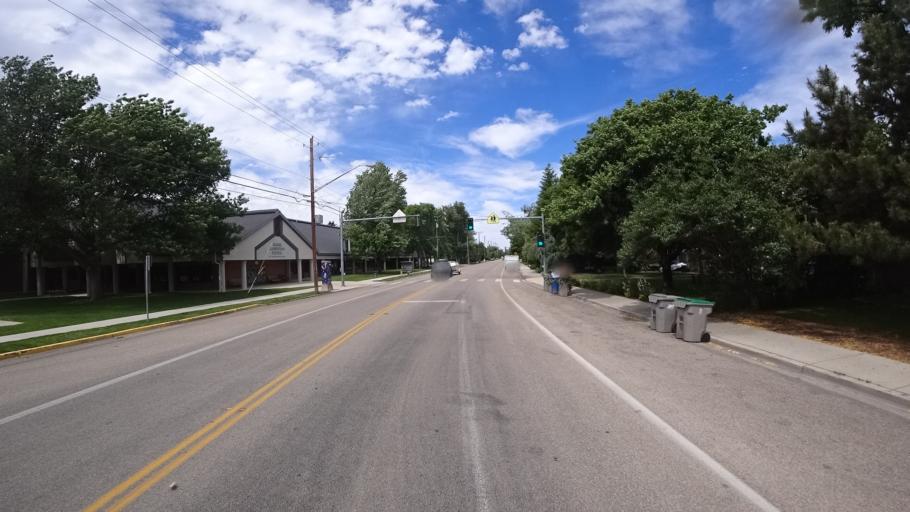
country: US
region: Idaho
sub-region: Ada County
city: Boise
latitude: 43.6031
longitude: -116.1732
